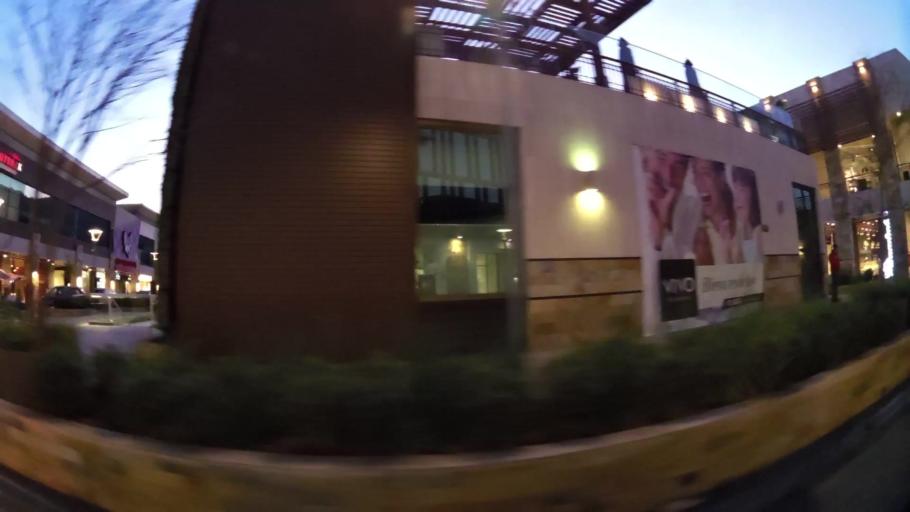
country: CL
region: Santiago Metropolitan
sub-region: Provincia de Santiago
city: Villa Presidente Frei, Nunoa, Santiago, Chile
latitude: -33.3567
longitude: -70.5396
